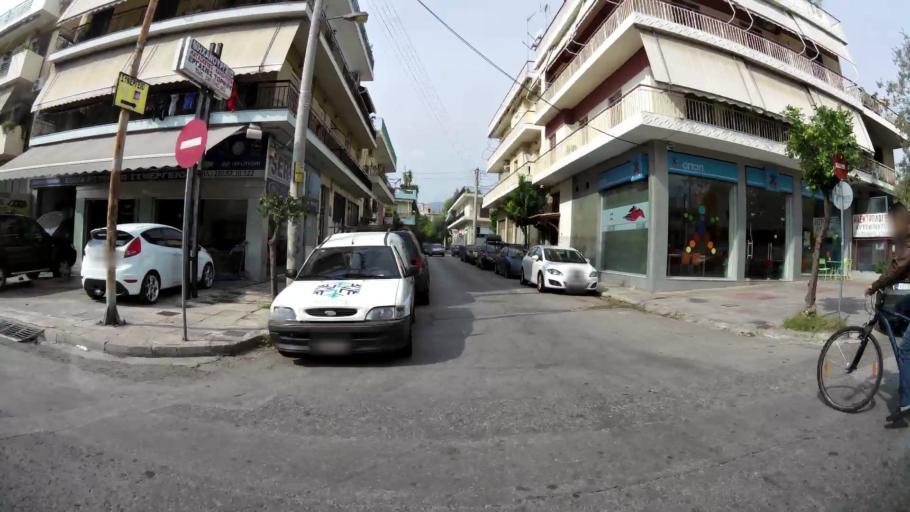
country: GR
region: Attica
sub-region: Nomarchia Athinas
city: Peristeri
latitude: 38.0151
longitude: 23.6878
